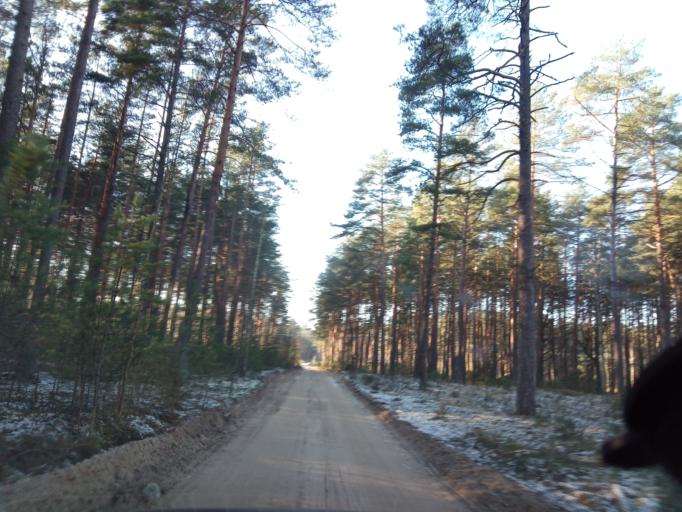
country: LT
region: Alytaus apskritis
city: Druskininkai
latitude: 53.9569
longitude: 23.8670
